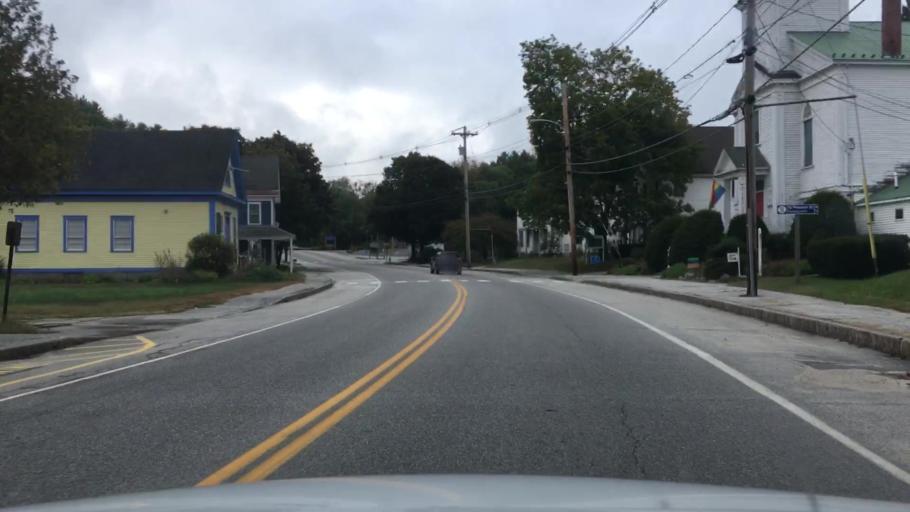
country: US
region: Maine
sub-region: Oxford County
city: Norway
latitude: 44.2141
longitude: -70.5441
